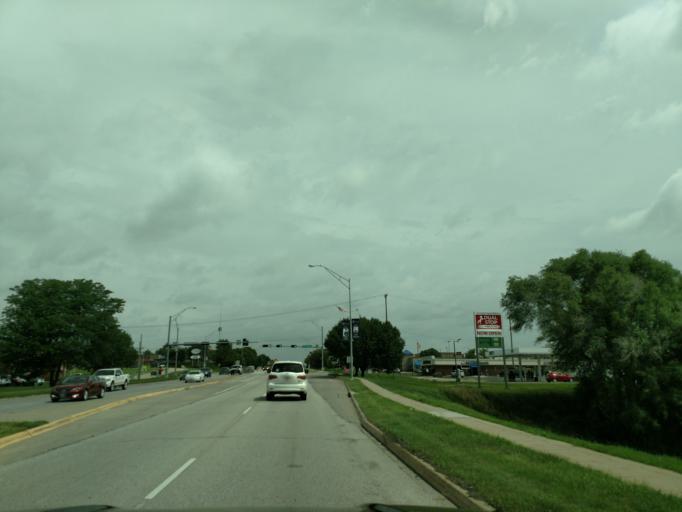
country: US
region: Nebraska
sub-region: Sarpy County
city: La Vista
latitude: 41.1866
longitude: -96.0429
